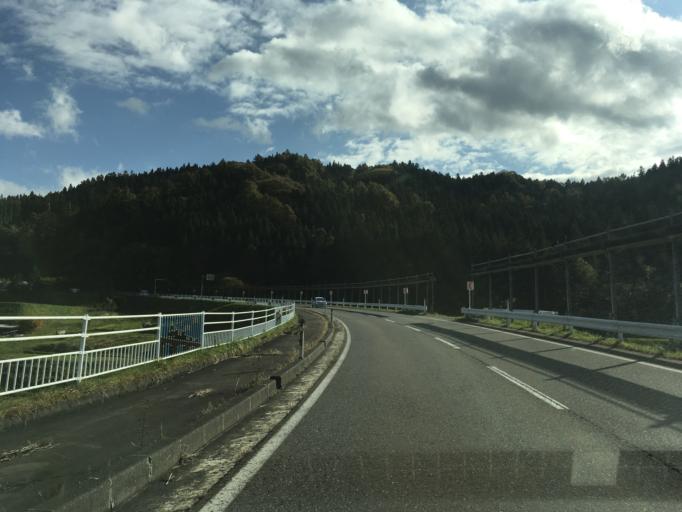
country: JP
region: Iwate
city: Tono
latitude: 39.3644
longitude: 141.4010
